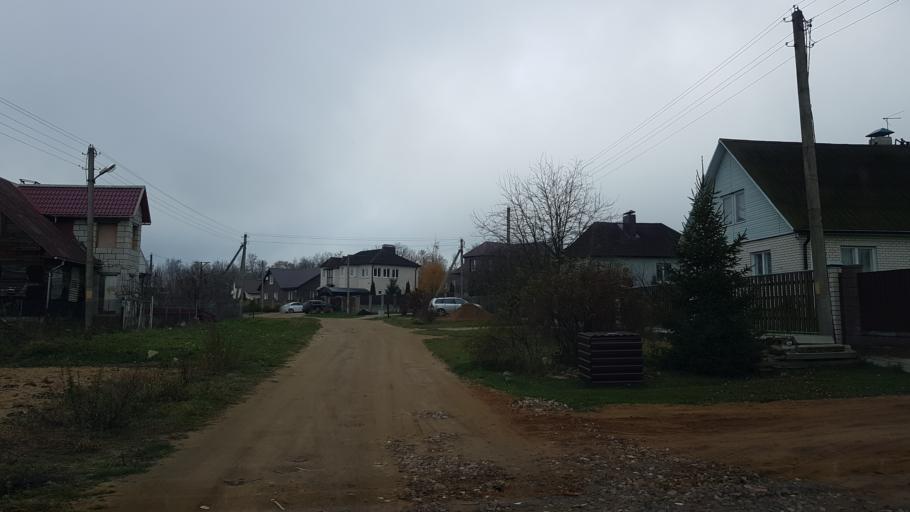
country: BY
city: Fanipol
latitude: 53.7310
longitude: 27.3151
